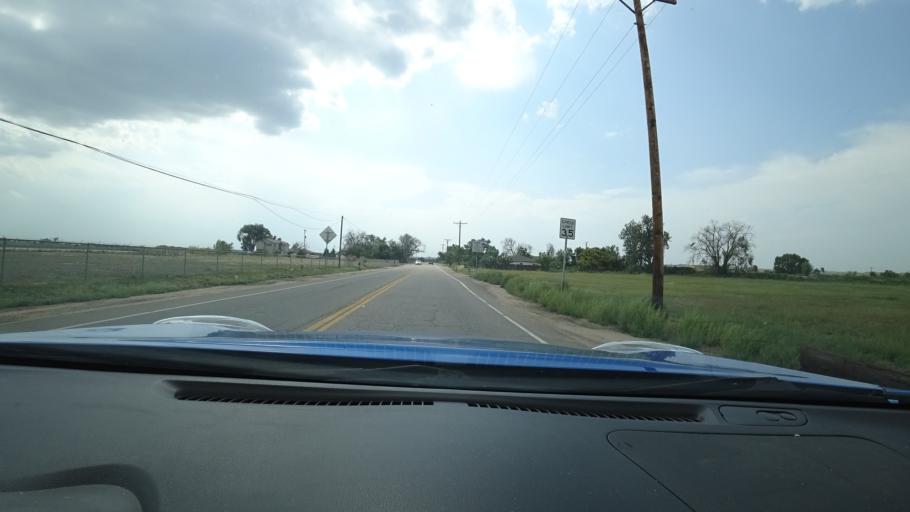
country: US
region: Colorado
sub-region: Adams County
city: Todd Creek
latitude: 39.9216
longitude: -104.8542
